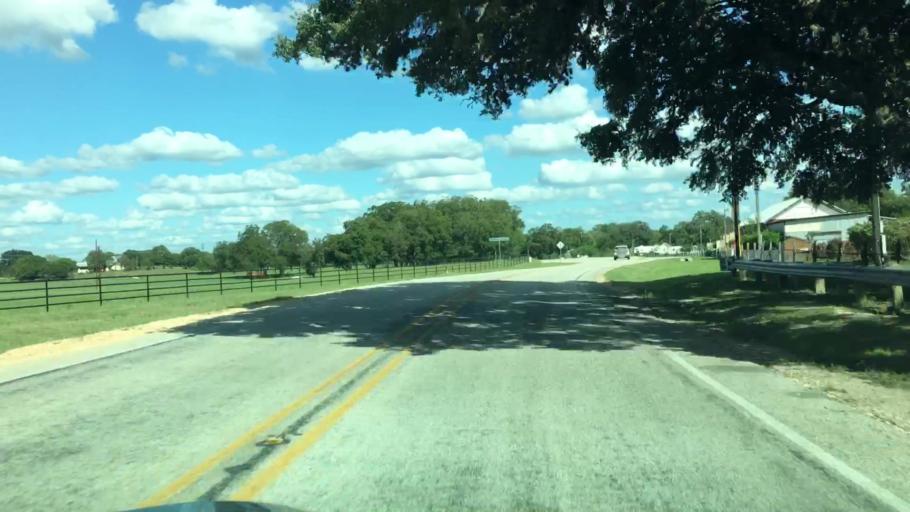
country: US
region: Texas
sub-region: Blanco County
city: Blanco
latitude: 30.0912
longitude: -98.3996
